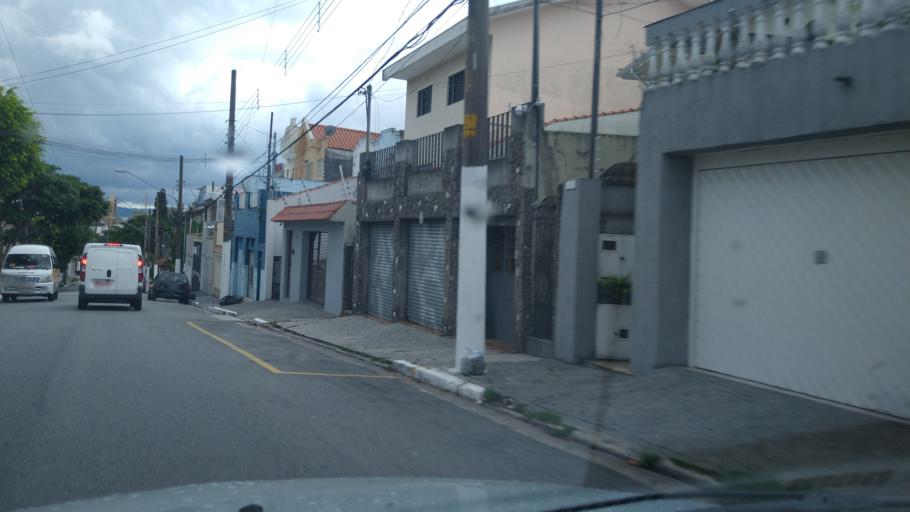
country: BR
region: Sao Paulo
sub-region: Sao Paulo
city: Sao Paulo
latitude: -23.5484
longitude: -46.5780
